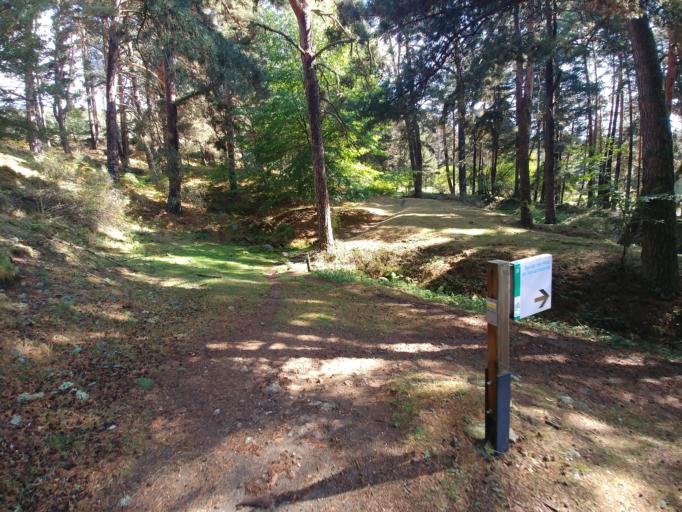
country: ES
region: Castille and Leon
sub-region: Provincia de Avila
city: Navarredonda de Gredos
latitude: 40.3533
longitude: -5.1091
